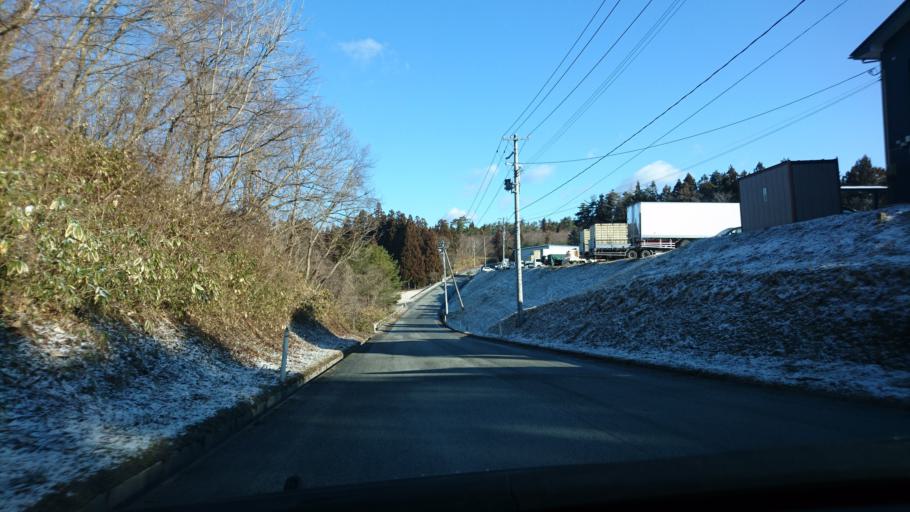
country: JP
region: Iwate
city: Ichinoseki
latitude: 38.8843
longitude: 141.3363
